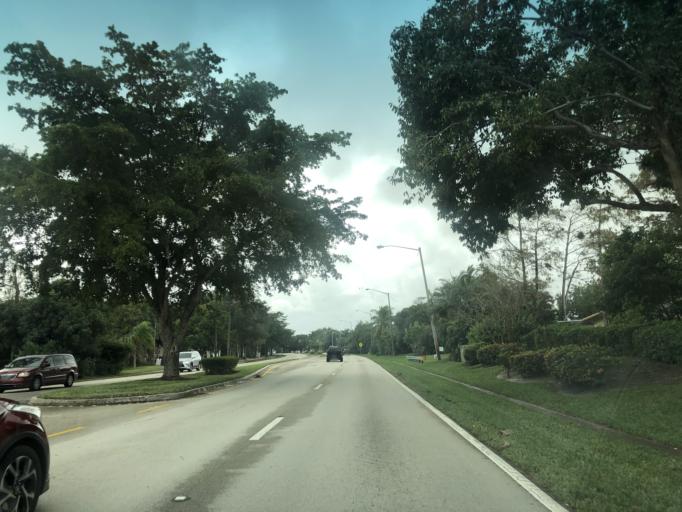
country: US
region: Florida
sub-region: Broward County
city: Margate
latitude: 26.2493
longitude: -80.2416
